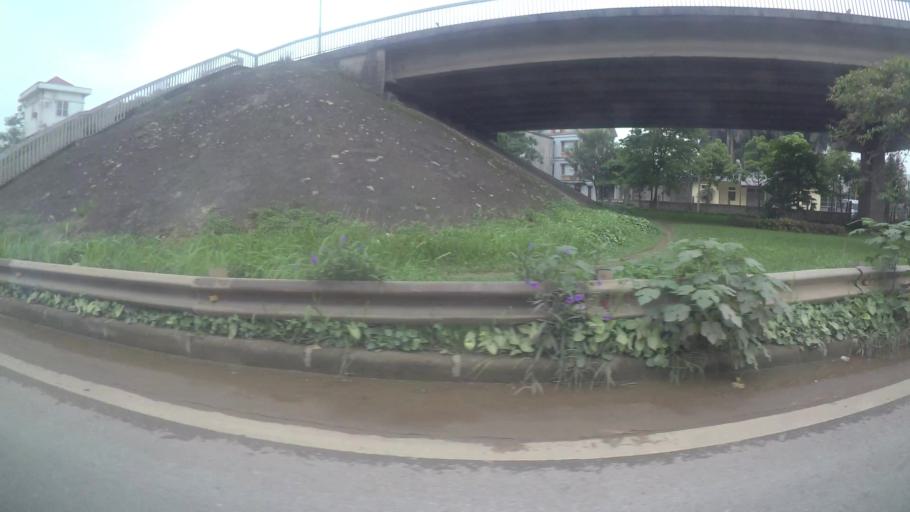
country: VN
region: Ha Noi
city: Tay Ho
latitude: 21.0853
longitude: 105.7875
